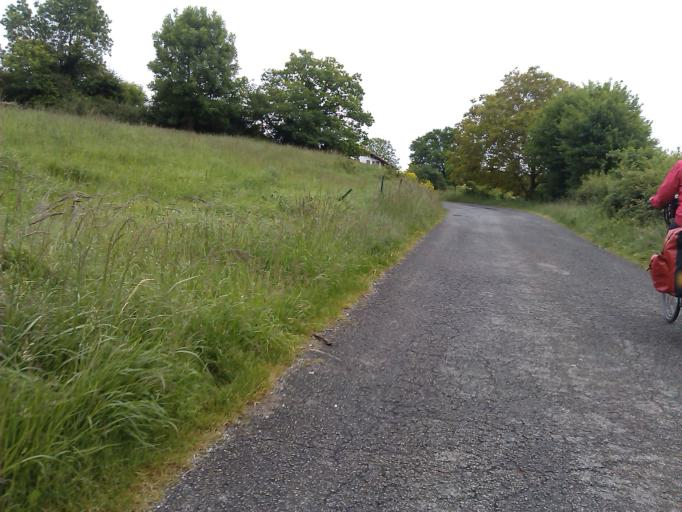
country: ES
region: Navarre
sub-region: Provincia de Navarra
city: Lekunberri
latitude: 42.9947
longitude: -1.8880
